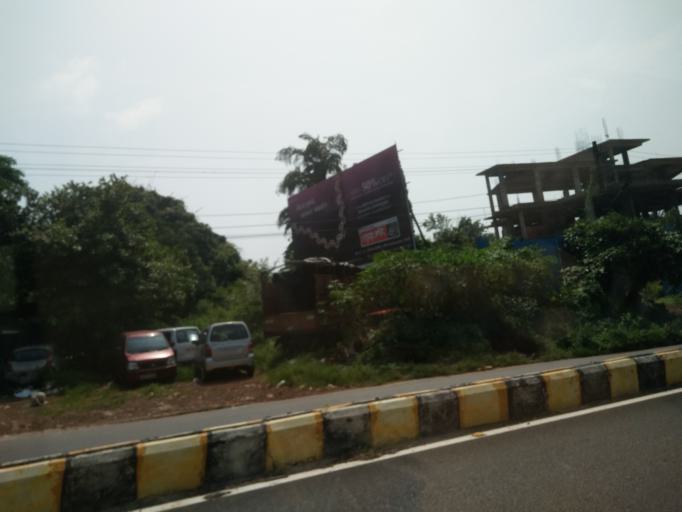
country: IN
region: Goa
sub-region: North Goa
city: Bambolim
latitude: 15.4647
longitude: 73.8545
